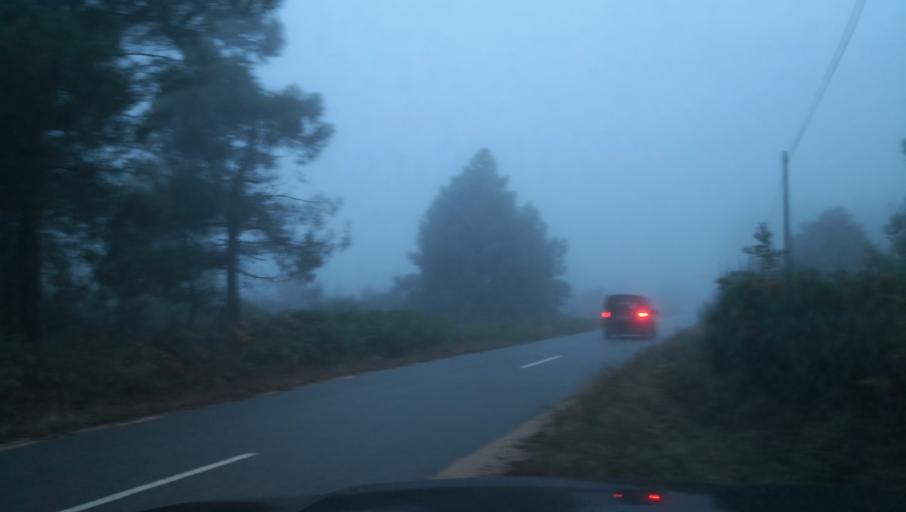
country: PT
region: Vila Real
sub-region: Sabrosa
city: Sabrosa
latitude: 41.2881
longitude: -7.6024
